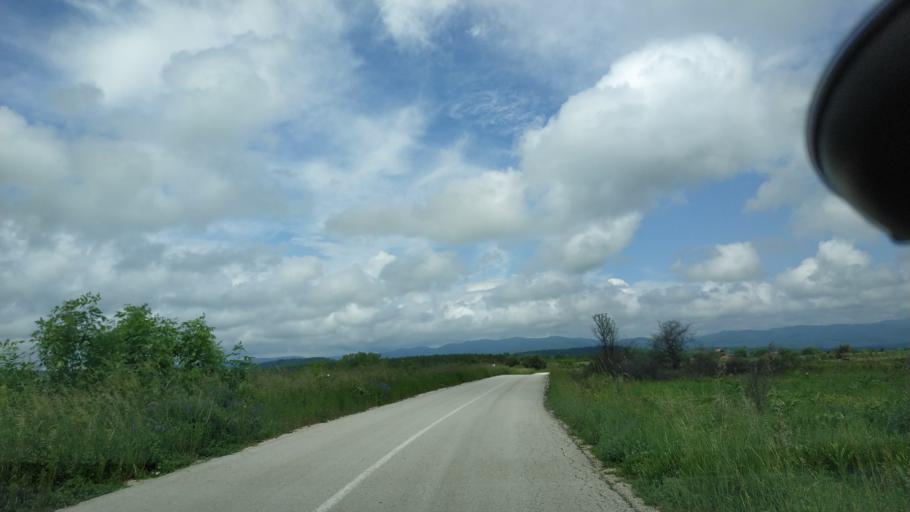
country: RS
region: Central Serbia
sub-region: Zajecarski Okrug
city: Boljevac
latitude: 43.8134
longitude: 21.9536
